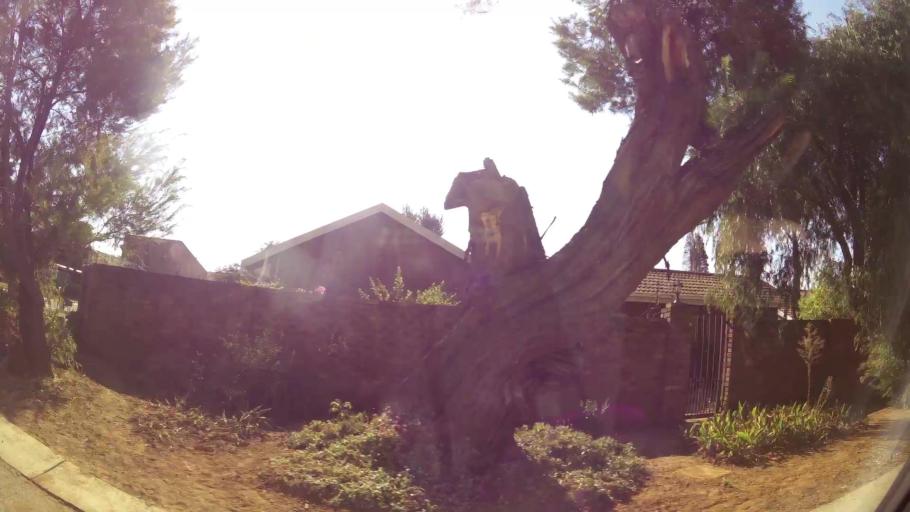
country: ZA
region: Gauteng
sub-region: Ekurhuleni Metropolitan Municipality
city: Boksburg
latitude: -26.1823
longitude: 28.2822
